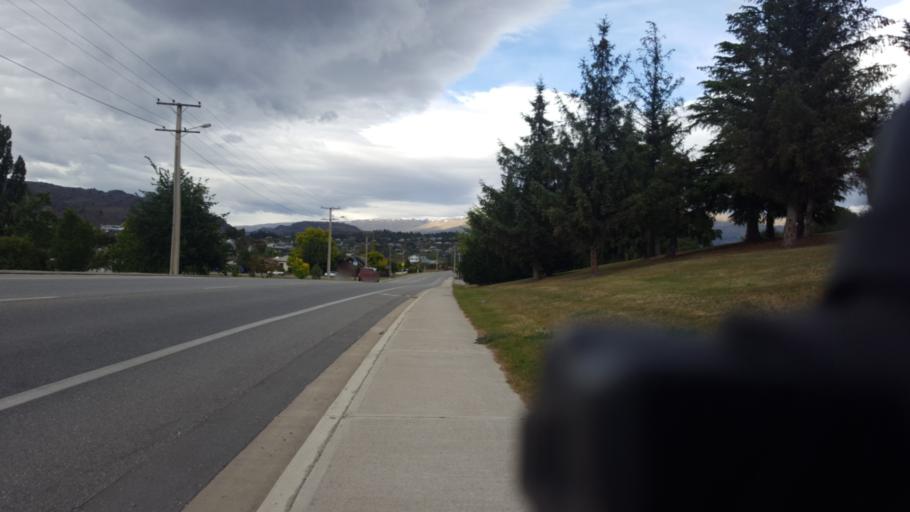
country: NZ
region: Otago
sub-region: Queenstown-Lakes District
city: Wanaka
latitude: -45.2470
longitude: 169.4015
